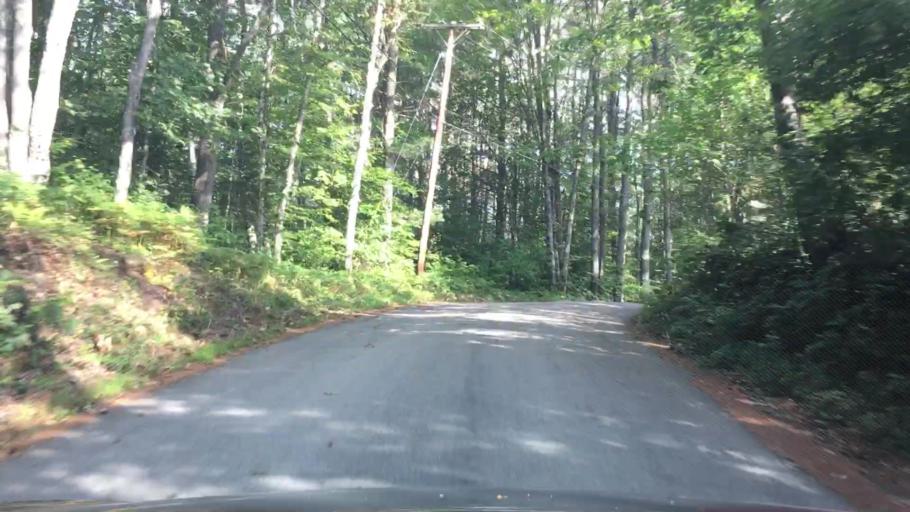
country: US
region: New Hampshire
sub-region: Grafton County
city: Littleton
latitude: 44.3131
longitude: -71.8817
